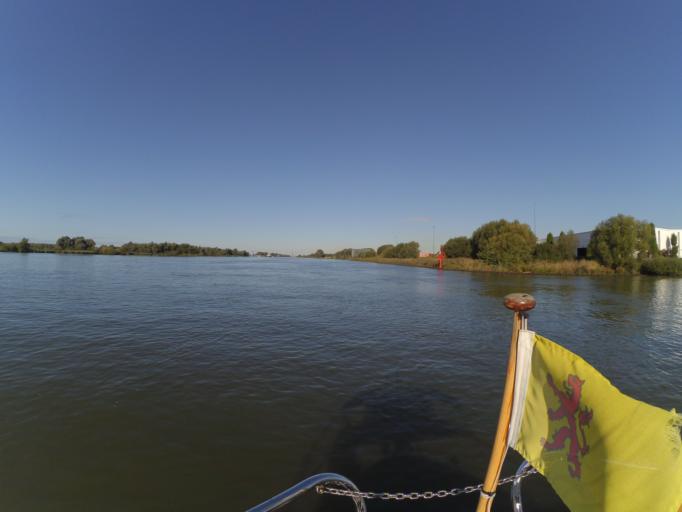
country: NL
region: South Holland
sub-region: Gemeente Zwijndrecht
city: Zwijndrecht
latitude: 51.8055
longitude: 4.6056
